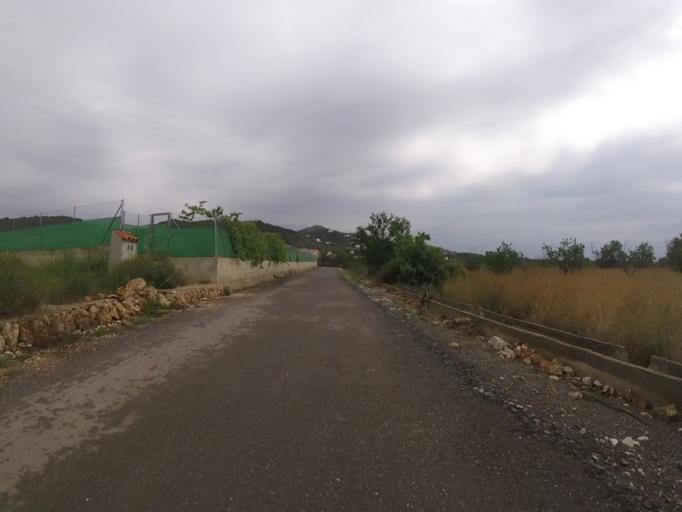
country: ES
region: Valencia
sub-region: Provincia de Castello
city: Alcoceber
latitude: 40.2451
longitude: 0.2545
